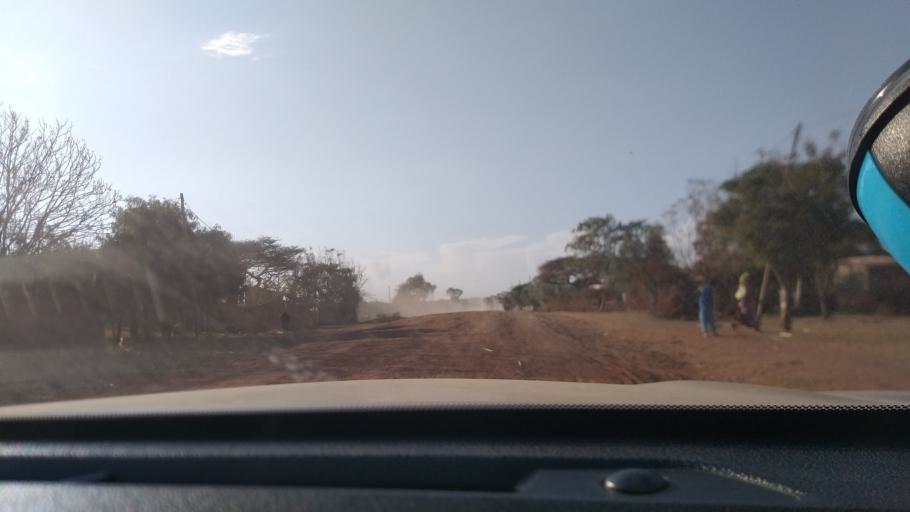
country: ET
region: Oromiya
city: Shashemene
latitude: 7.4884
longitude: 38.7225
